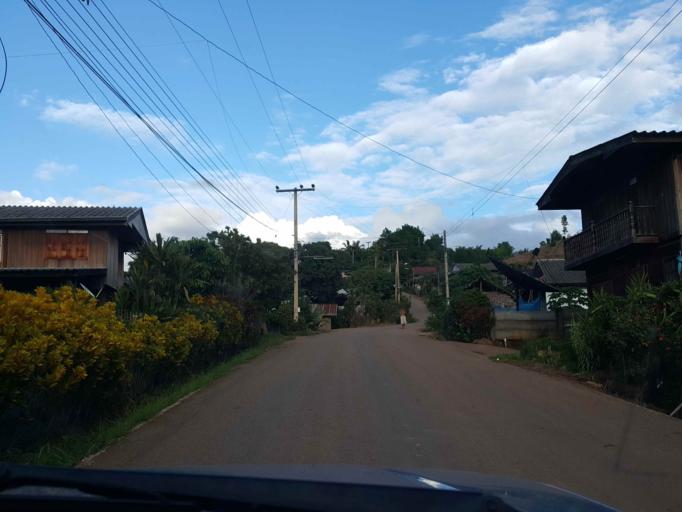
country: TH
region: Chiang Mai
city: Mae Chaem
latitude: 18.5146
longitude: 98.4004
